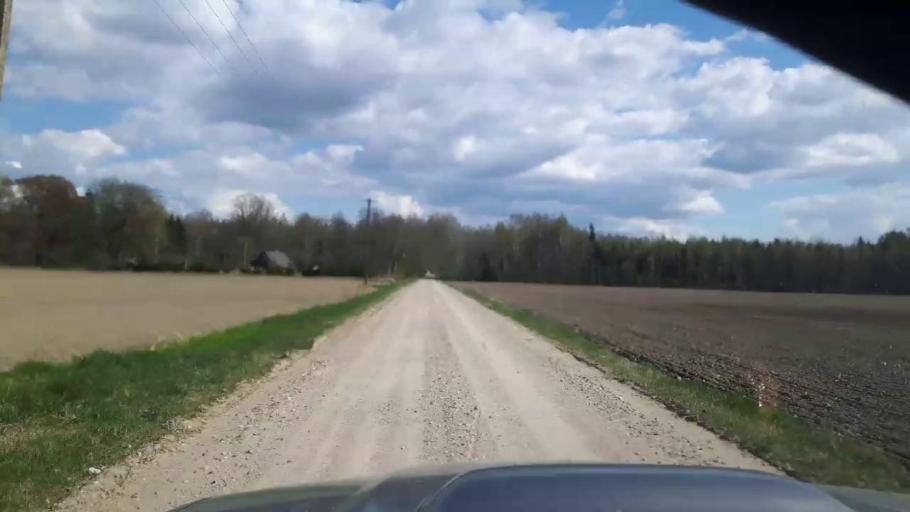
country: EE
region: Paernumaa
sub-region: Tootsi vald
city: Tootsi
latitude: 58.4558
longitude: 24.8154
